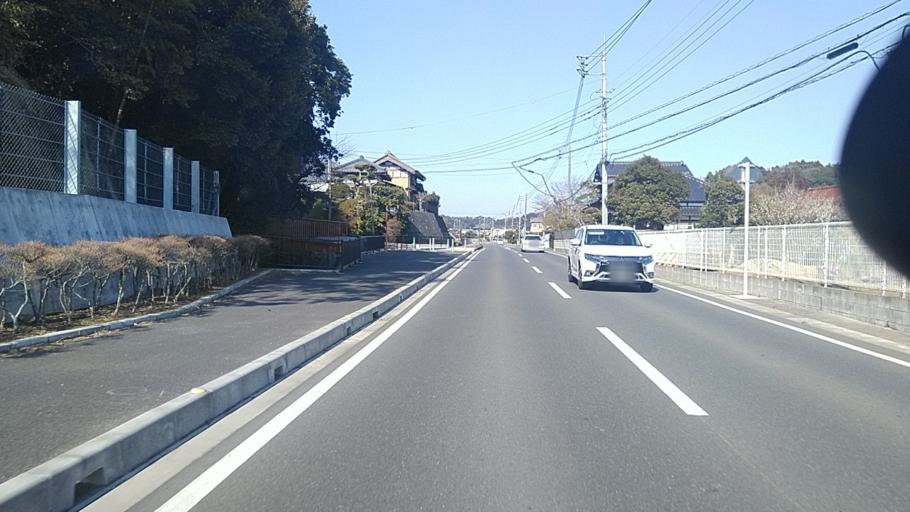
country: JP
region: Chiba
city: Oami
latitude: 35.4748
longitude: 140.2806
